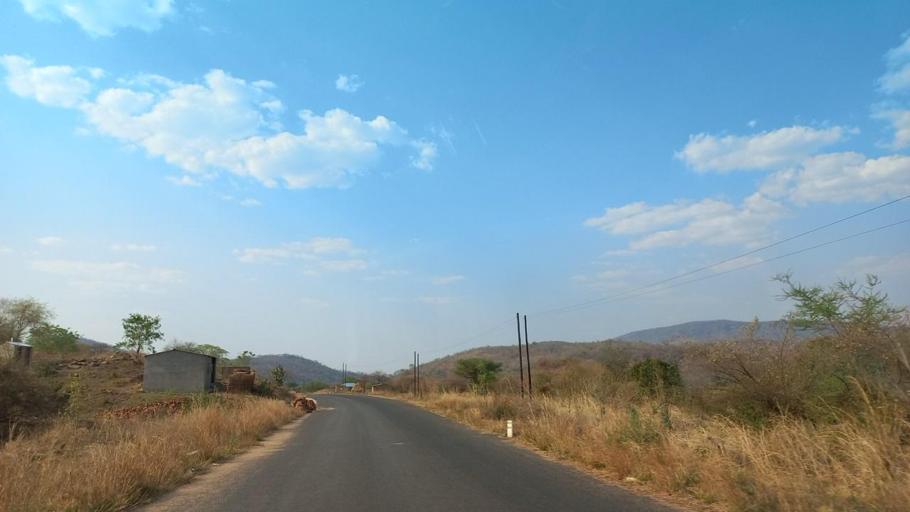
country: ZM
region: Lusaka
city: Luangwa
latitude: -14.9937
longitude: 30.2135
